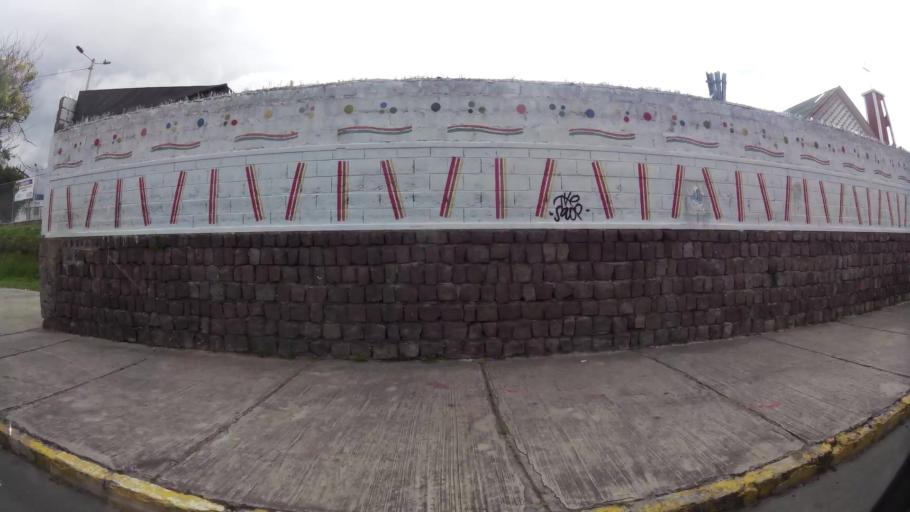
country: EC
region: Pichincha
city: Quito
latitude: -0.1440
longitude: -78.4962
